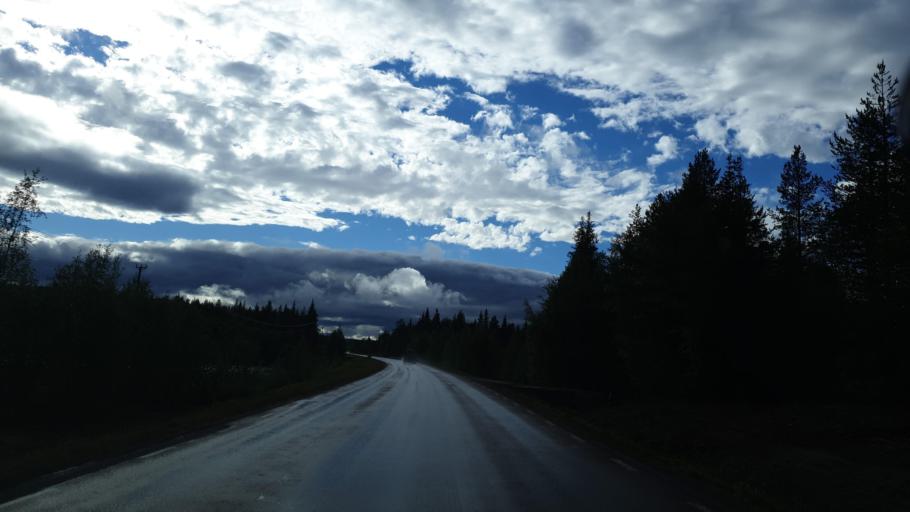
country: SE
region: Norrbotten
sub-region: Arjeplogs Kommun
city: Arjeplog
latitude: 66.0512
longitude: 18.0189
